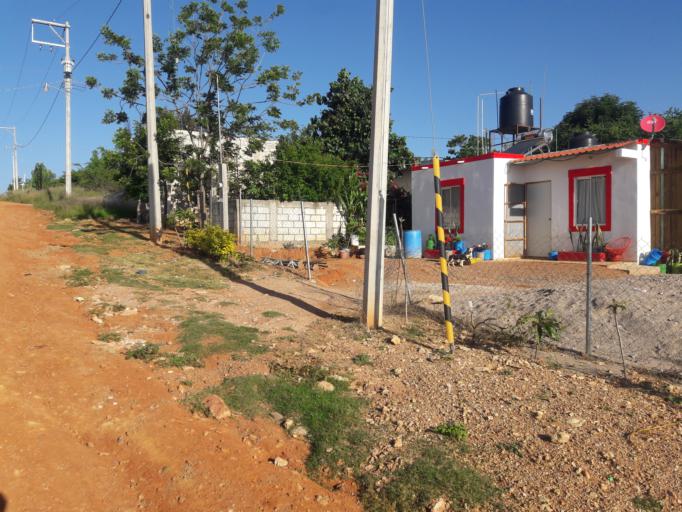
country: MX
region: Oaxaca
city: San Jeronimo Silacayoapilla
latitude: 17.8022
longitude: -97.8157
